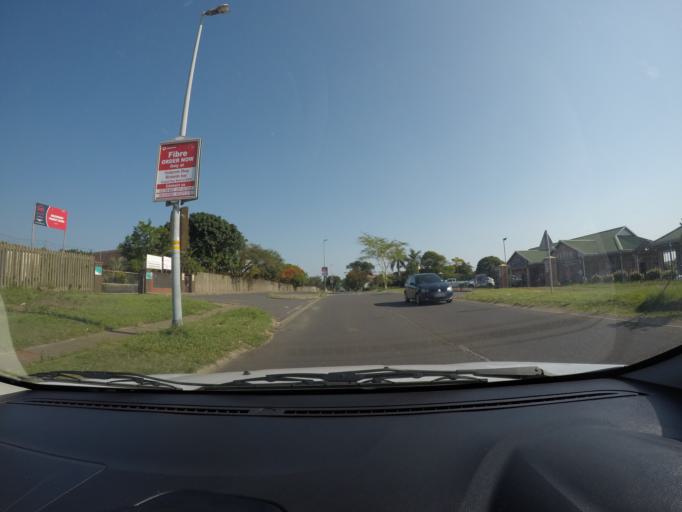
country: ZA
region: KwaZulu-Natal
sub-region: uThungulu District Municipality
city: Richards Bay
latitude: -28.7229
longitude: 32.0412
